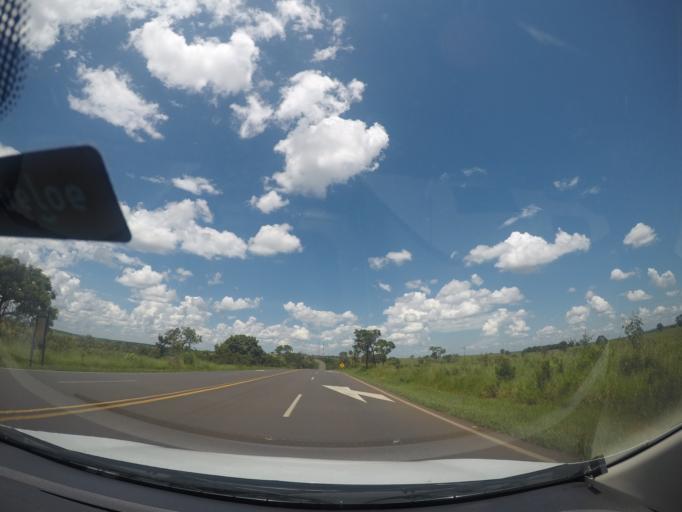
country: BR
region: Minas Gerais
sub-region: Prata
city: Prata
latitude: -19.1493
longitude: -48.9624
